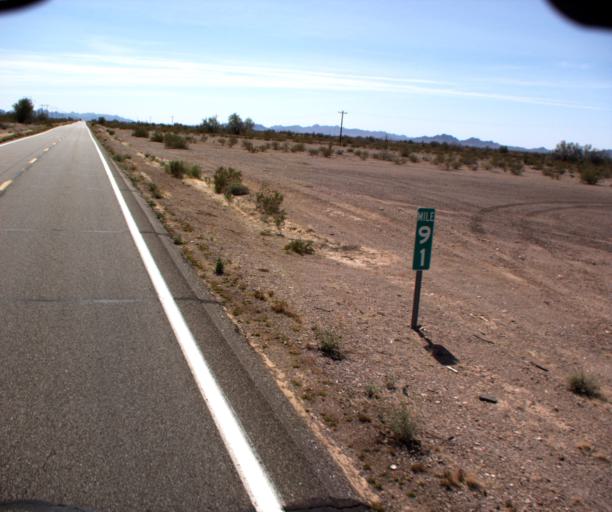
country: US
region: Arizona
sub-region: La Paz County
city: Quartzsite
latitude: 33.4708
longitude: -114.2170
